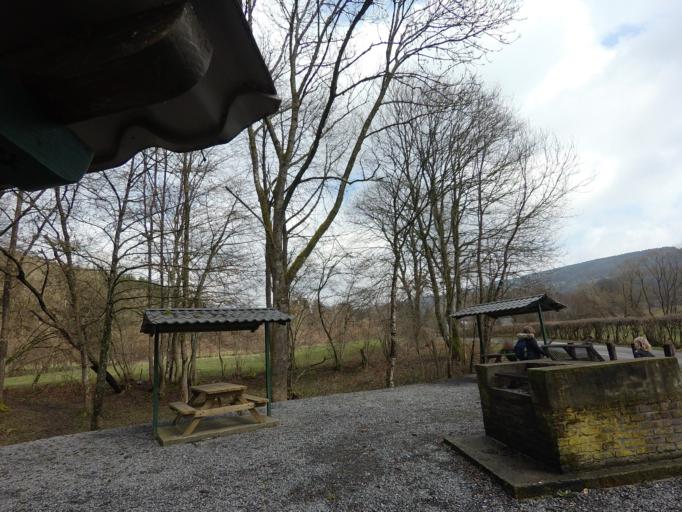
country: BE
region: Wallonia
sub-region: Province de Liege
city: Trois-Ponts
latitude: 50.4258
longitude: 5.8827
